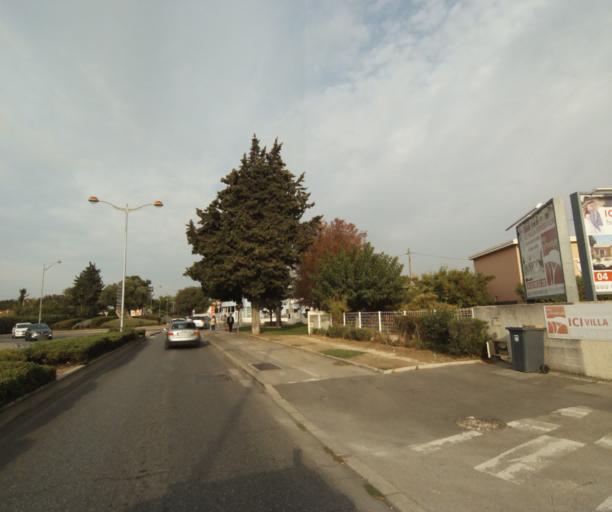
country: FR
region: Provence-Alpes-Cote d'Azur
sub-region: Departement des Bouches-du-Rhone
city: Marignane
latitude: 43.4133
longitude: 5.2212
